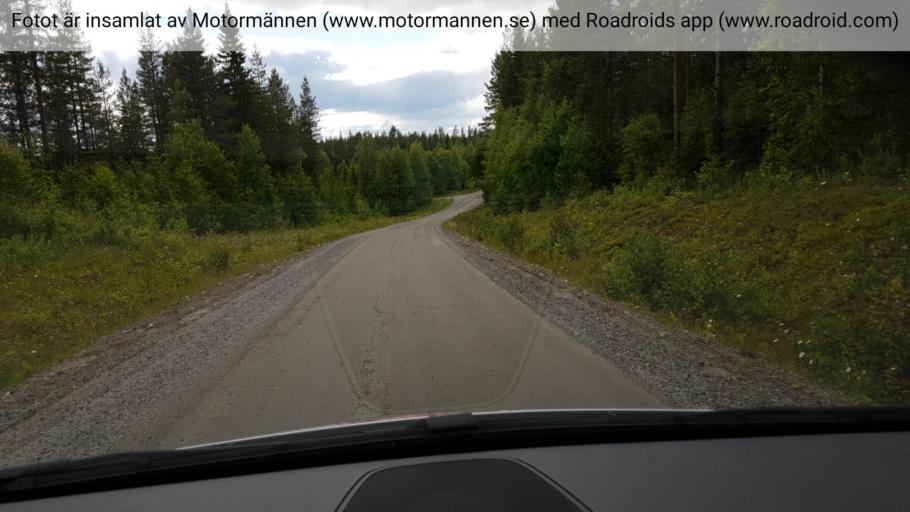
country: SE
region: Vaesterbotten
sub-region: Dorotea Kommun
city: Dorotea
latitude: 63.9305
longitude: 16.1477
